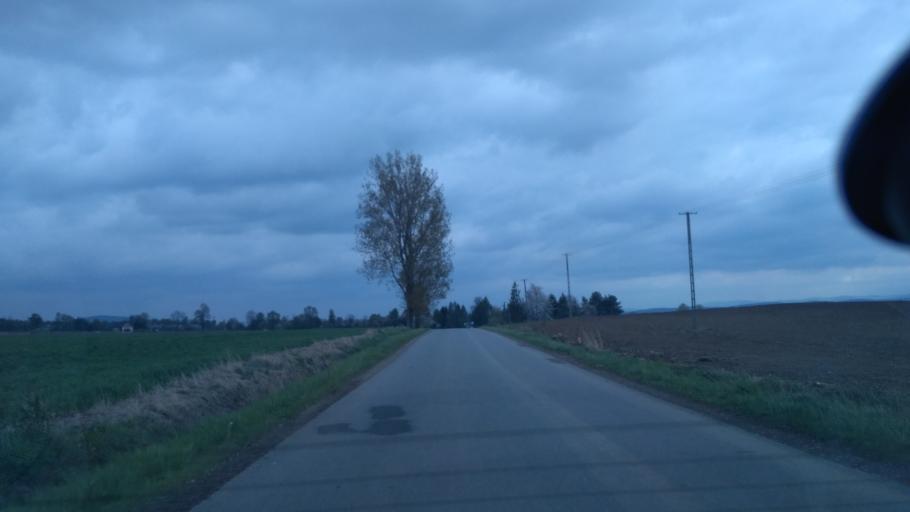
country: PL
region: Subcarpathian Voivodeship
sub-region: Powiat brzozowski
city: Turze Pole
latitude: 49.6303
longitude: 22.0081
